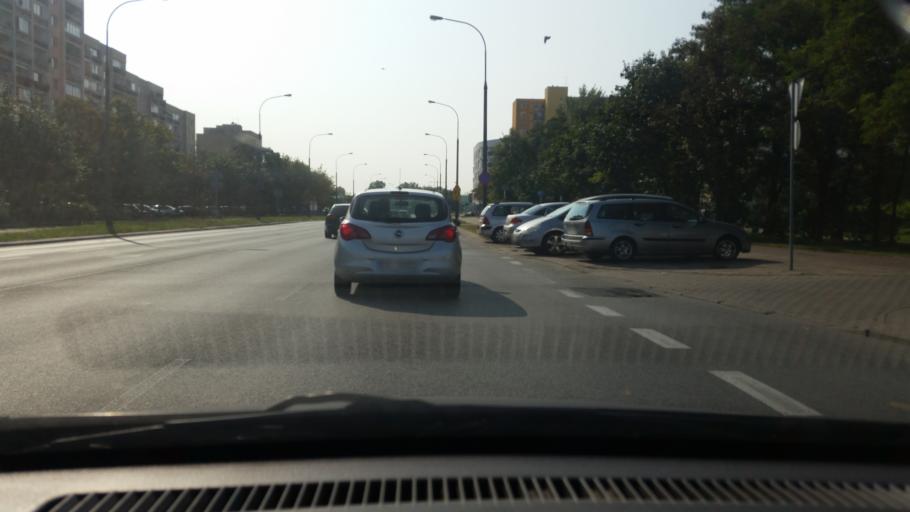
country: PL
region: Masovian Voivodeship
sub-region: Warszawa
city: Bialoleka
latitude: 52.3163
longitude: 20.9611
